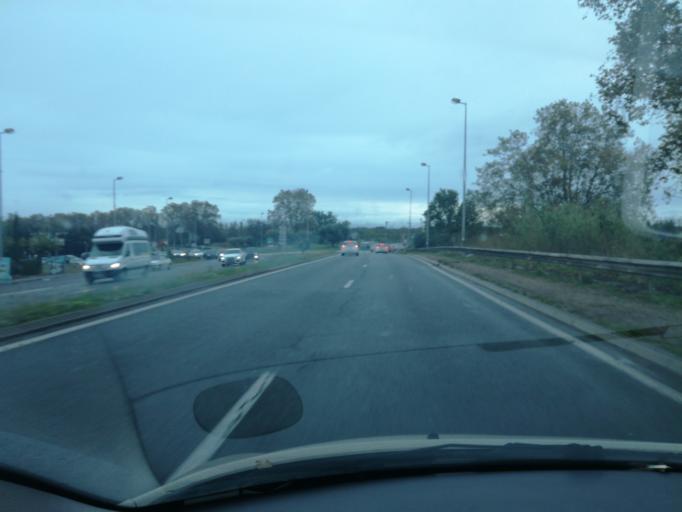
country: FR
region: Provence-Alpes-Cote d'Azur
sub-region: Departement du Var
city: Puget-sur-Argens
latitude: 43.4403
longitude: 6.7064
